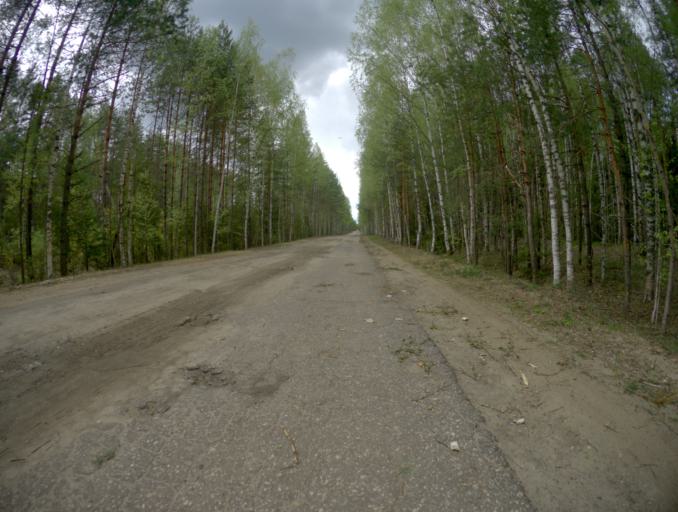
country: RU
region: Vladimir
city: Velikodvorskiy
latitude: 55.2434
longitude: 40.7329
